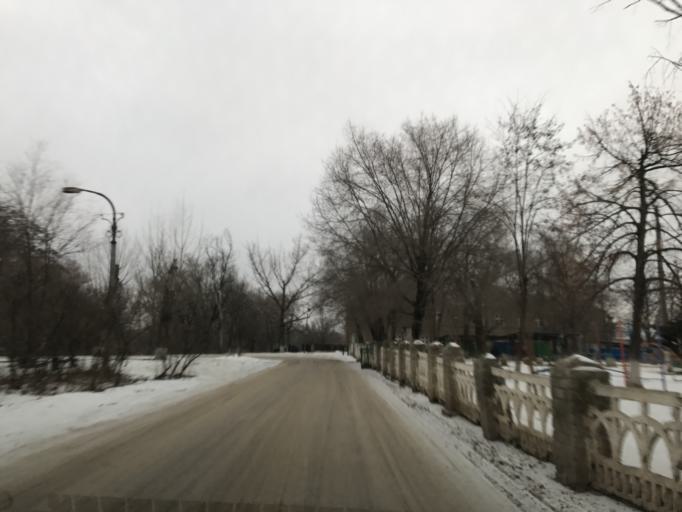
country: RU
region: Rostov
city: Kamensk-Shakhtinskiy
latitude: 48.3330
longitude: 40.2563
